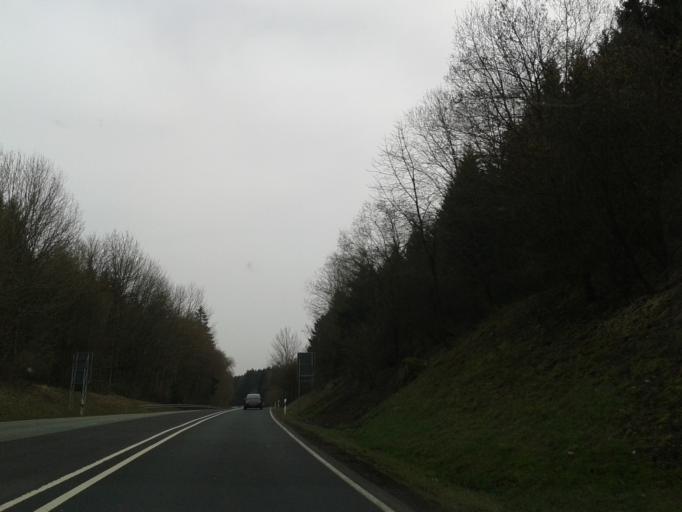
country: DE
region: Rheinland-Pfalz
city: Rehe
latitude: 50.6490
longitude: 8.1440
